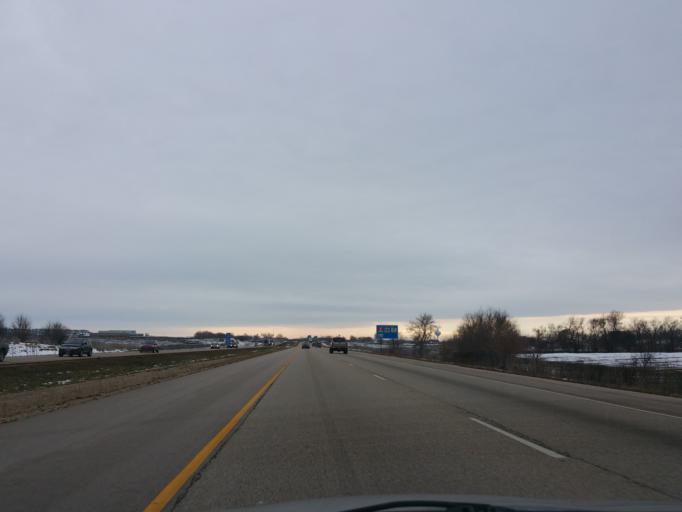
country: US
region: Wisconsin
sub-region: Rock County
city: Beloit
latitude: 42.5379
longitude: -88.9752
